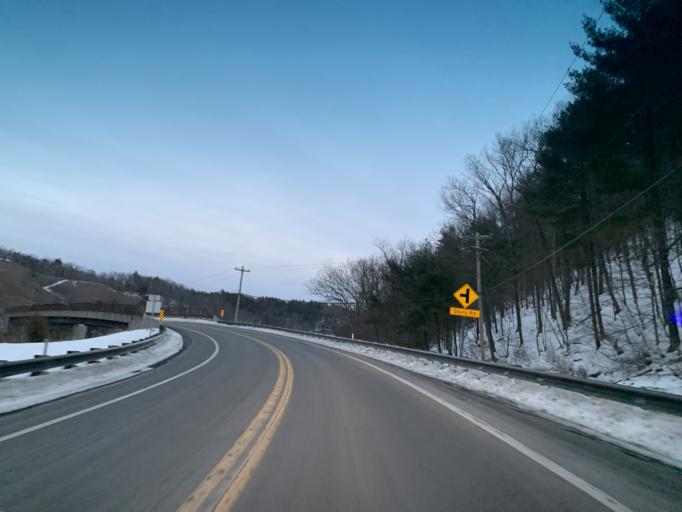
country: US
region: West Virginia
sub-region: Morgan County
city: Berkeley Springs
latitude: 39.6770
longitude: -78.4703
